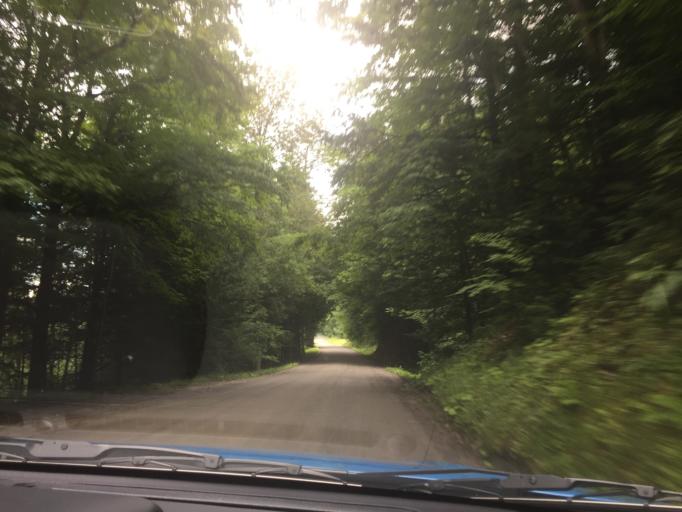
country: US
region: Vermont
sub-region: Windsor County
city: Woodstock
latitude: 43.7669
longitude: -72.4802
